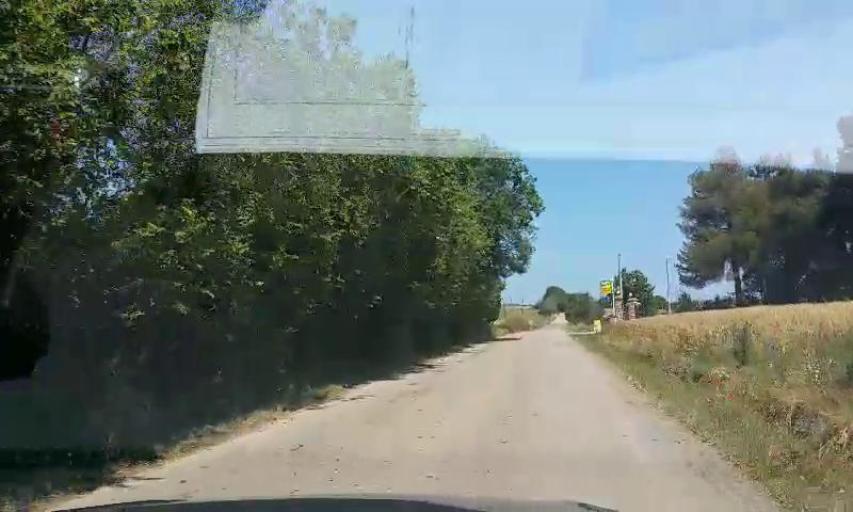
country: IT
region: Molise
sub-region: Provincia di Campobasso
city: Guglionesi
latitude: 41.9563
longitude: 14.9005
